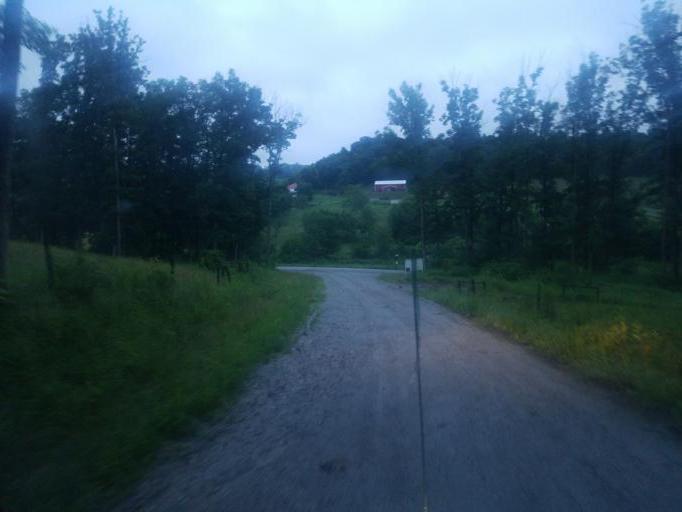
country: US
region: Ohio
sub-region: Carroll County
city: Carrollton
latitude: 40.5026
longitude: -81.0537
